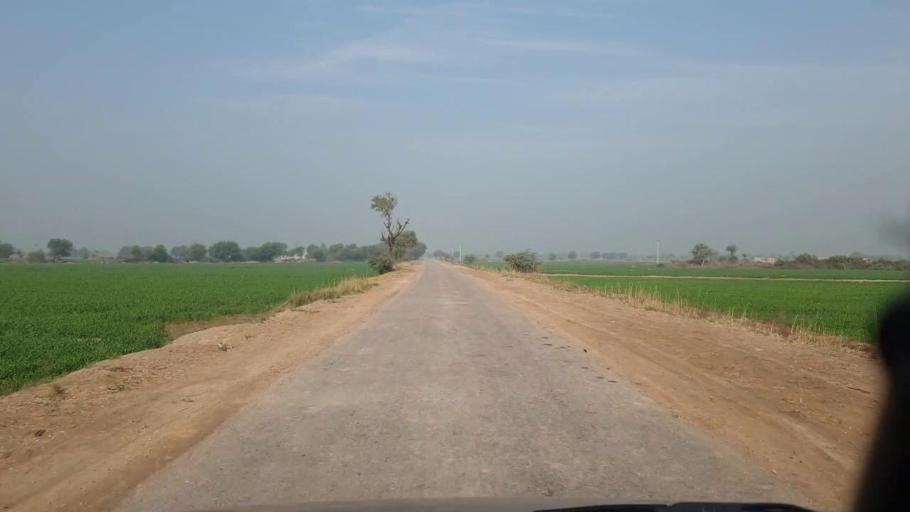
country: PK
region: Sindh
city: Shahdadpur
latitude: 25.9982
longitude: 68.5584
